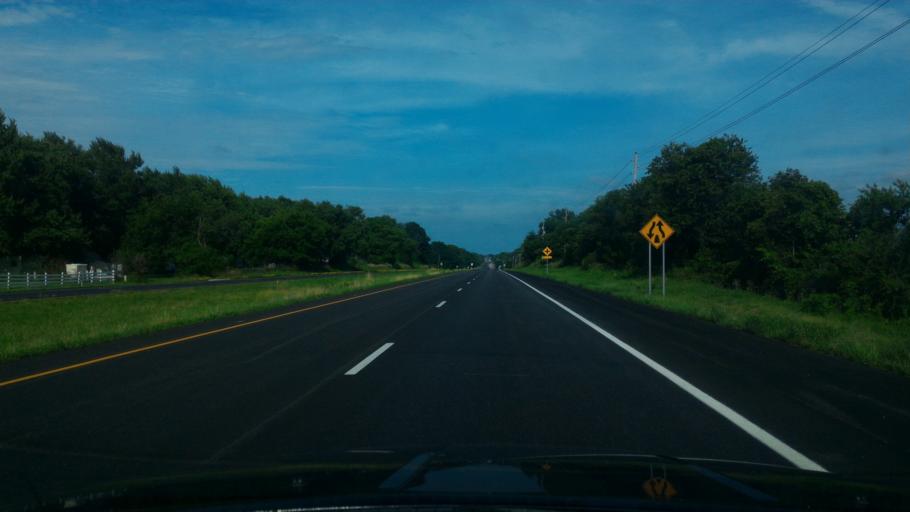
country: US
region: Indiana
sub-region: Tippecanoe County
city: West Lafayette
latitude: 40.4674
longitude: -86.9861
